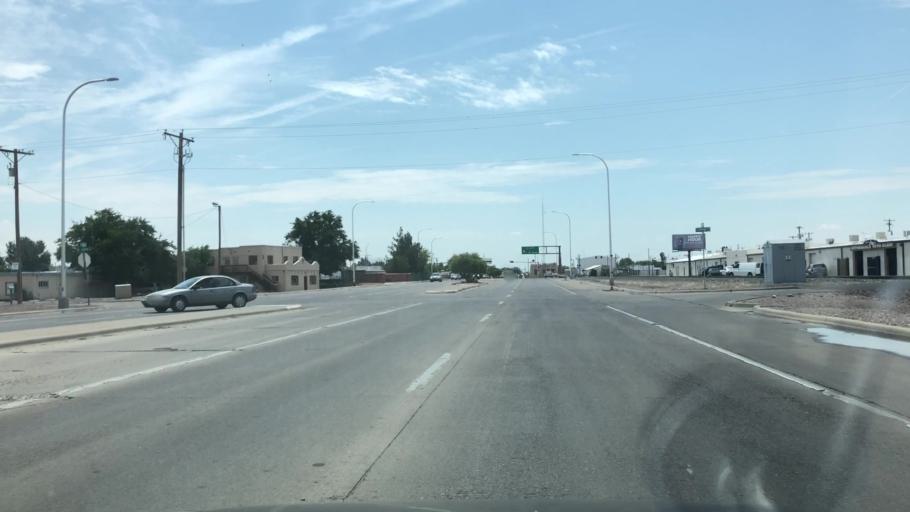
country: US
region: New Mexico
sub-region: Dona Ana County
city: University Park
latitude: 32.2797
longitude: -106.7694
